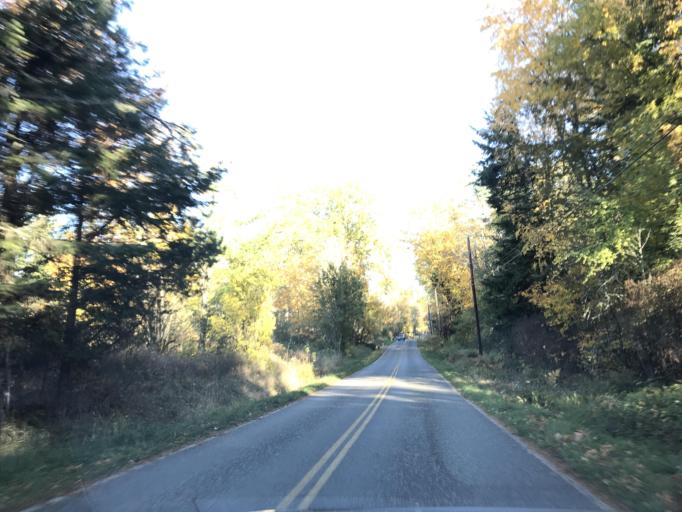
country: US
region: Washington
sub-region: Whatcom County
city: Geneva
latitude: 48.7678
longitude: -122.3925
